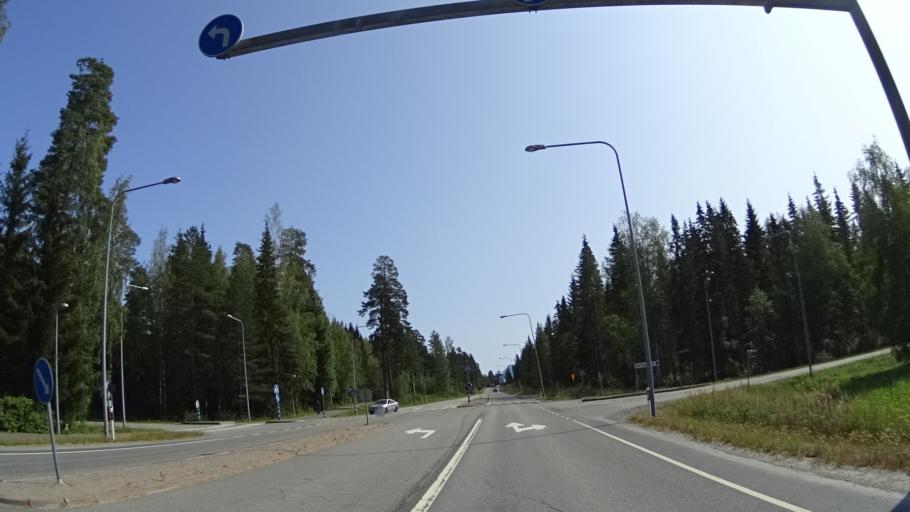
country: FI
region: Pirkanmaa
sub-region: Ylae-Pirkanmaa
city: Maenttae
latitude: 62.0285
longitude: 24.5973
